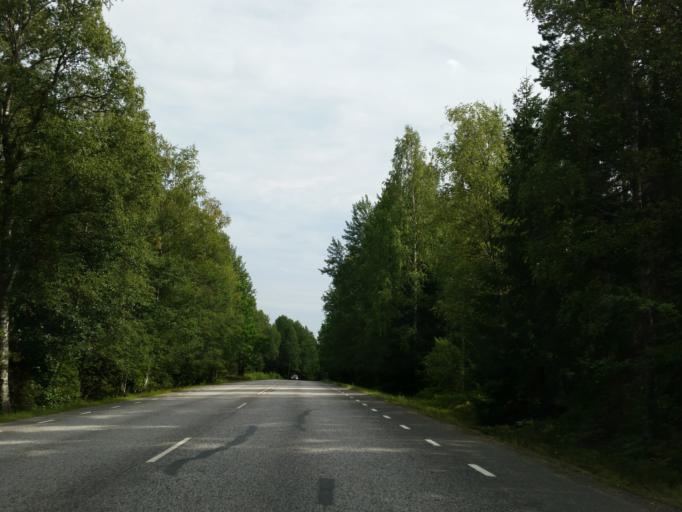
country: SE
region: Soedermanland
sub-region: Strangnas Kommun
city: Mariefred
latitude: 59.2320
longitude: 17.2083
